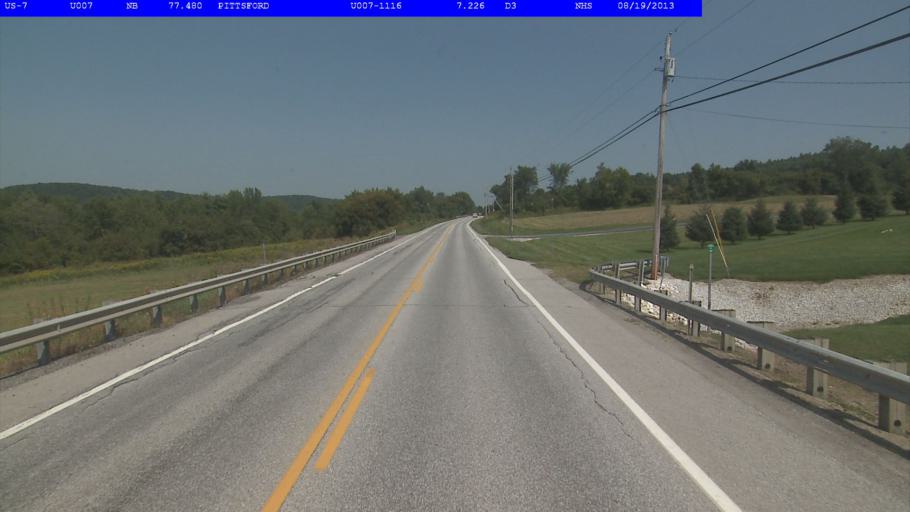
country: US
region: Vermont
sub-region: Rutland County
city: Brandon
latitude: 43.7491
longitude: -73.0475
